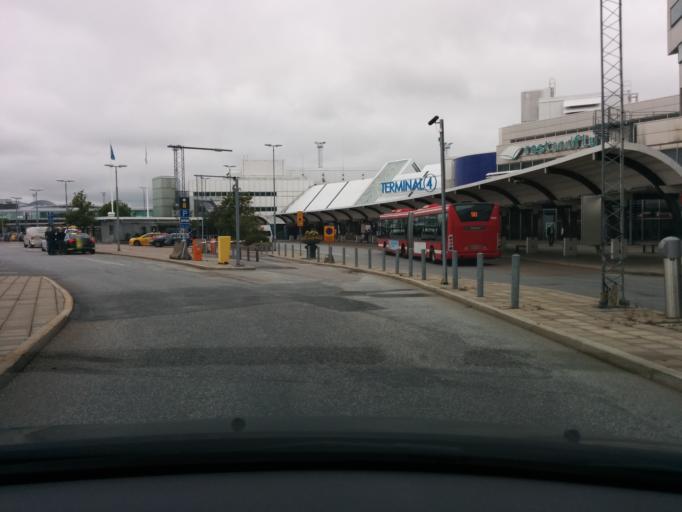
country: SE
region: Stockholm
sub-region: Sigtuna Kommun
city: Marsta
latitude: 59.6484
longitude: 17.9295
